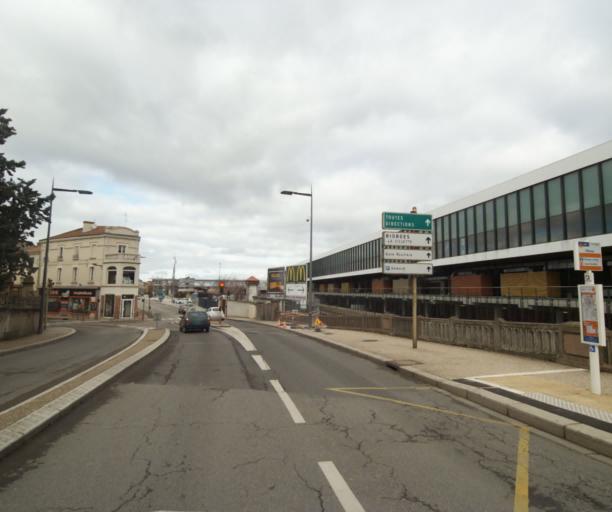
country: FR
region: Rhone-Alpes
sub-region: Departement de la Loire
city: Roanne
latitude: 46.0369
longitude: 4.0641
